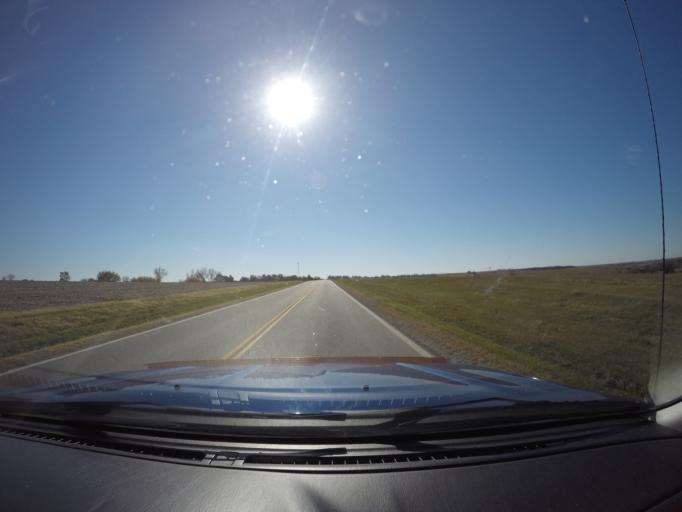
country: US
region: Kansas
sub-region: Marshall County
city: Marysville
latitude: 39.8517
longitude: -96.4171
